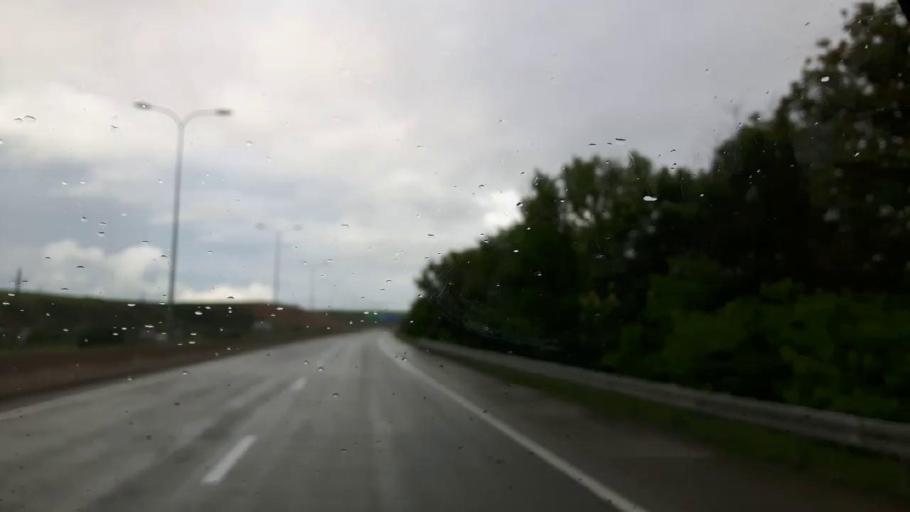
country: GE
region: Shida Kartli
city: Kaspi
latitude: 42.0008
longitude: 44.3845
